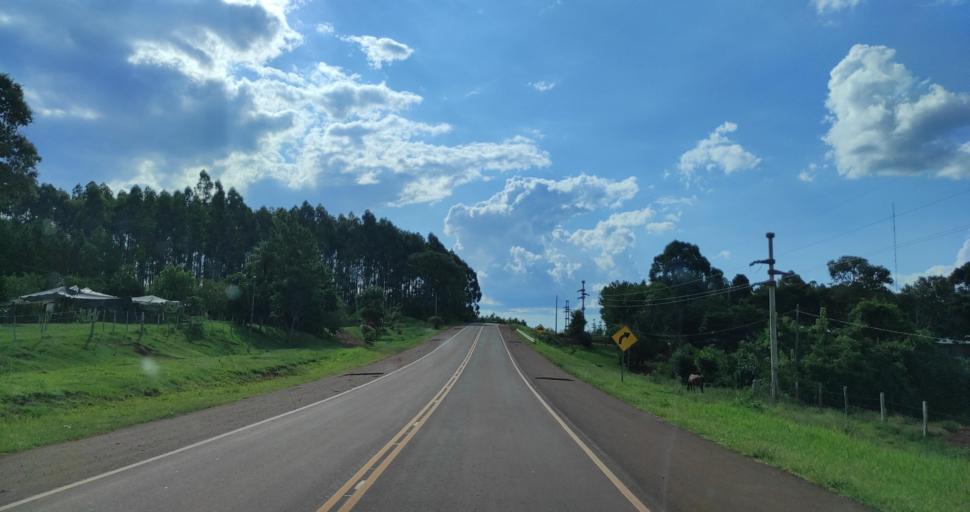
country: AR
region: Misiones
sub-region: Departamento de San Pedro
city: San Pedro
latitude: -26.3696
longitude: -53.9417
